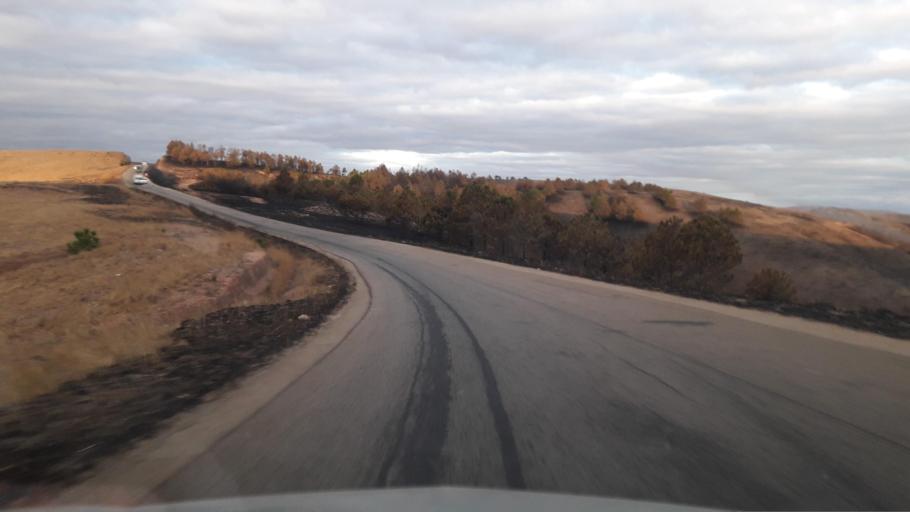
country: MG
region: Analamanga
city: Ankazobe
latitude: -17.8795
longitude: 47.0414
